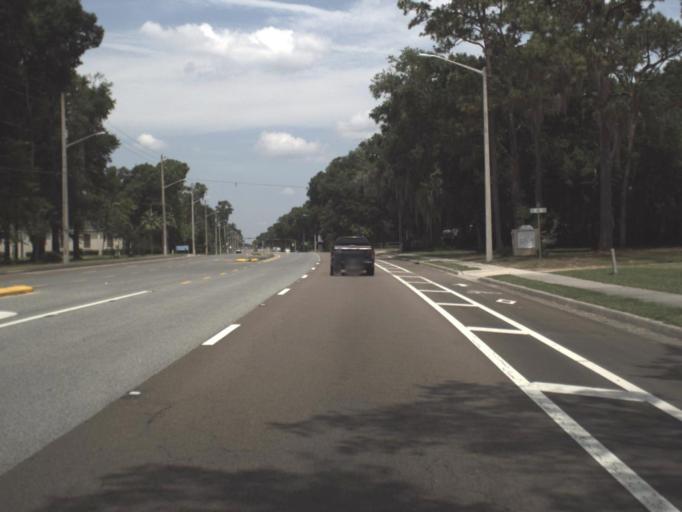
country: US
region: Florida
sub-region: Alachua County
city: Gainesville
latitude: 29.6334
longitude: -82.2683
